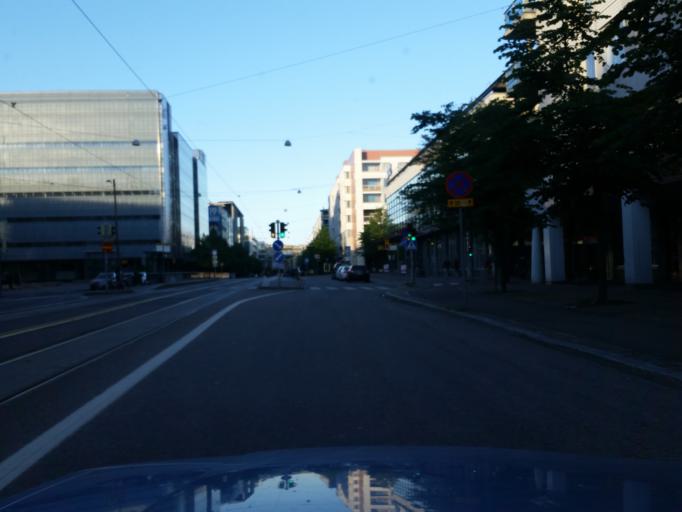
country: FI
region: Uusimaa
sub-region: Helsinki
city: Helsinki
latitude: 60.1633
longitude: 24.9132
